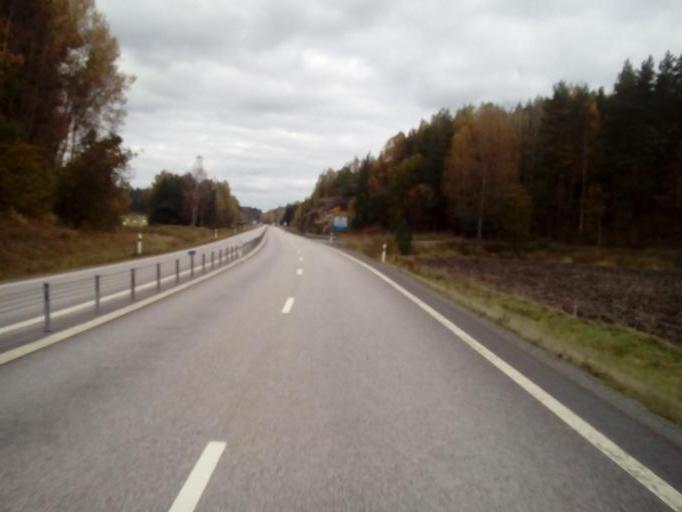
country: SE
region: OEstergoetland
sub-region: Valdemarsviks Kommun
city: Valdemarsvik
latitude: 58.2022
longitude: 16.5562
